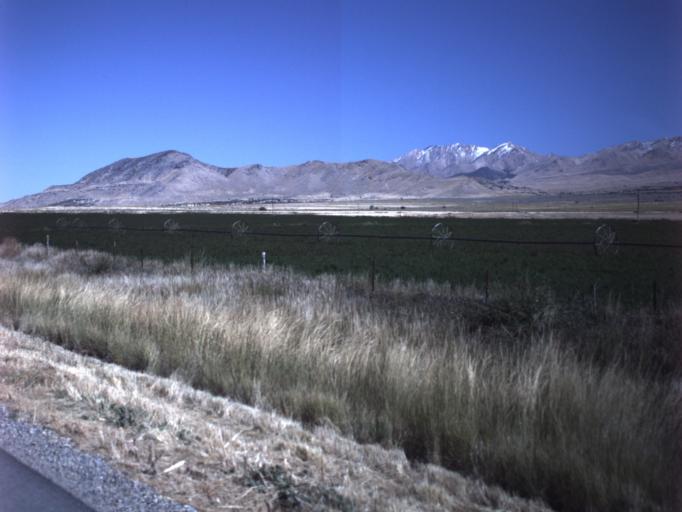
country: US
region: Utah
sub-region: Tooele County
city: Grantsville
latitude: 40.4963
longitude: -112.7480
